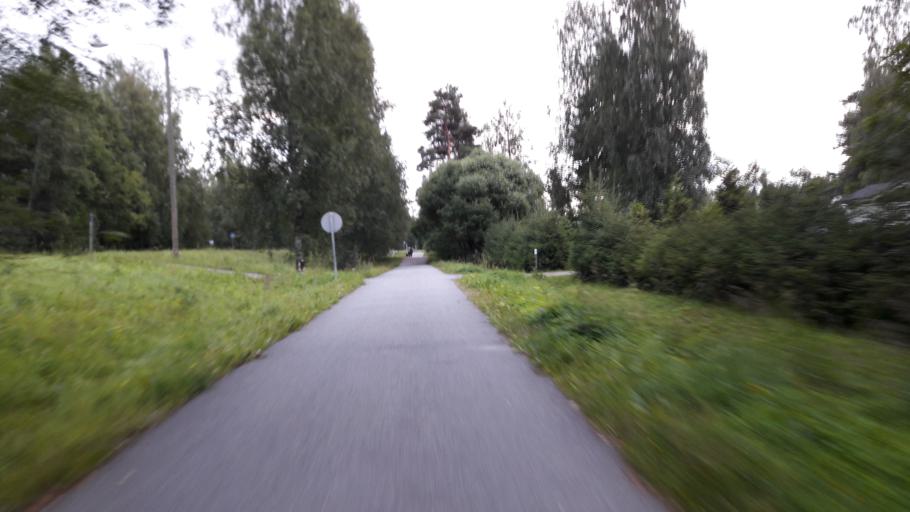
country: FI
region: North Karelia
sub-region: Joensuu
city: Joensuu
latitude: 62.5522
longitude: 29.8244
